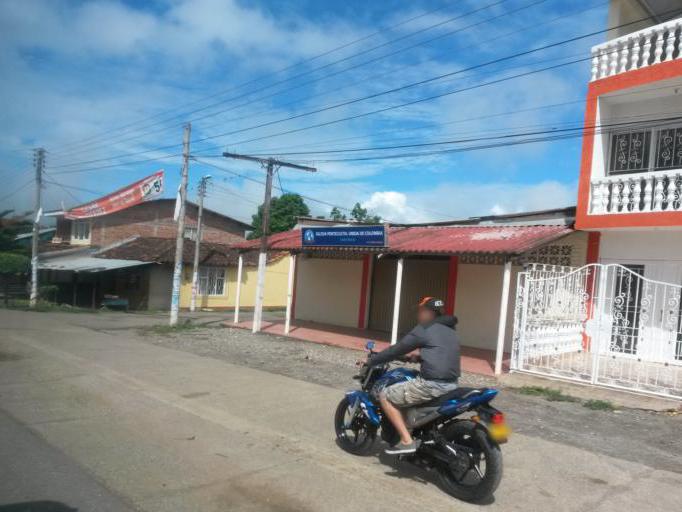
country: CO
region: Cauca
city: El Bordo
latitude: 2.1253
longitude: -76.9763
